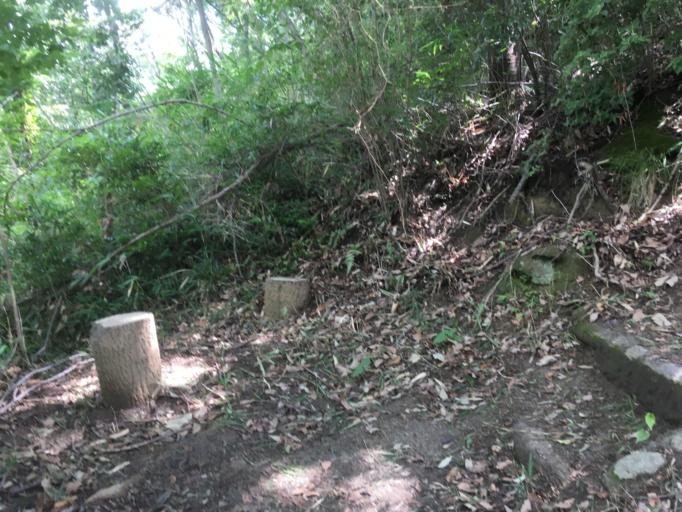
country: JP
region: Nara
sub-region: Ikoma-shi
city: Ikoma
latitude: 34.6904
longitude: 135.6623
